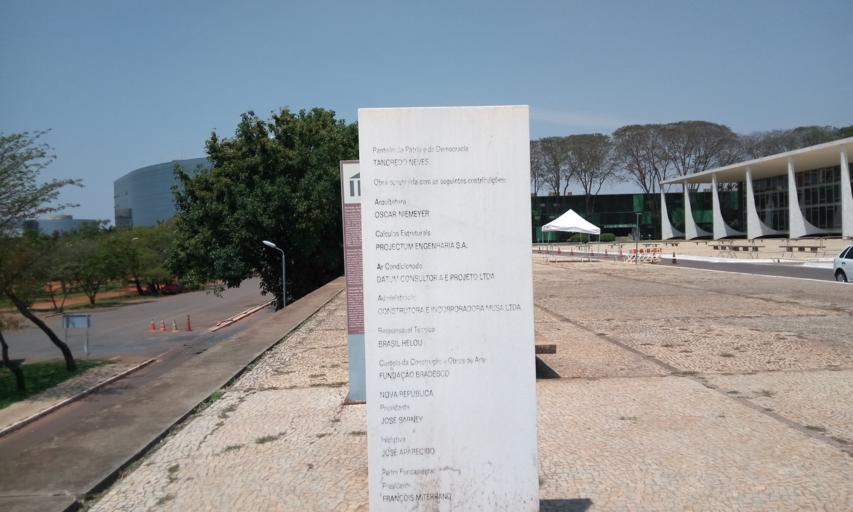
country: BR
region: Federal District
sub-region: Brasilia
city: Brasilia
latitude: -15.8015
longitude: -47.8607
